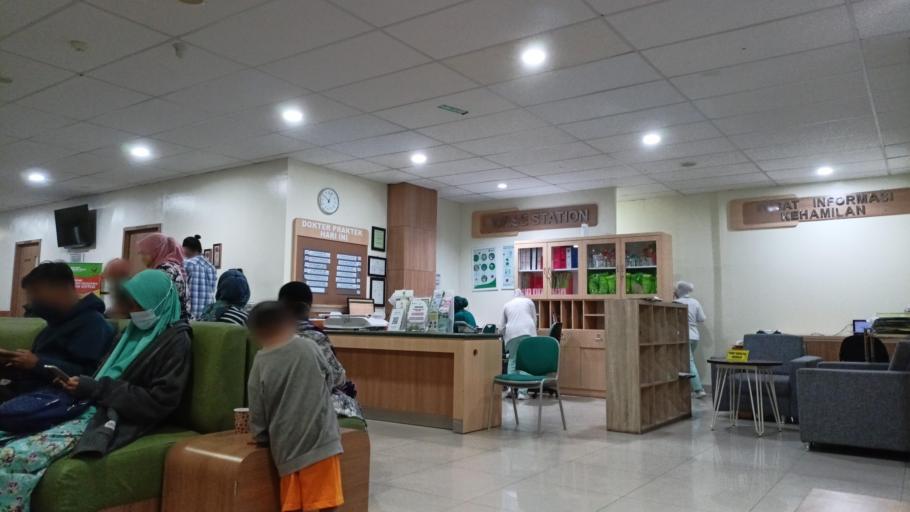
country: ID
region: Central Java
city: Surakarta
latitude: -7.5603
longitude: 110.8403
